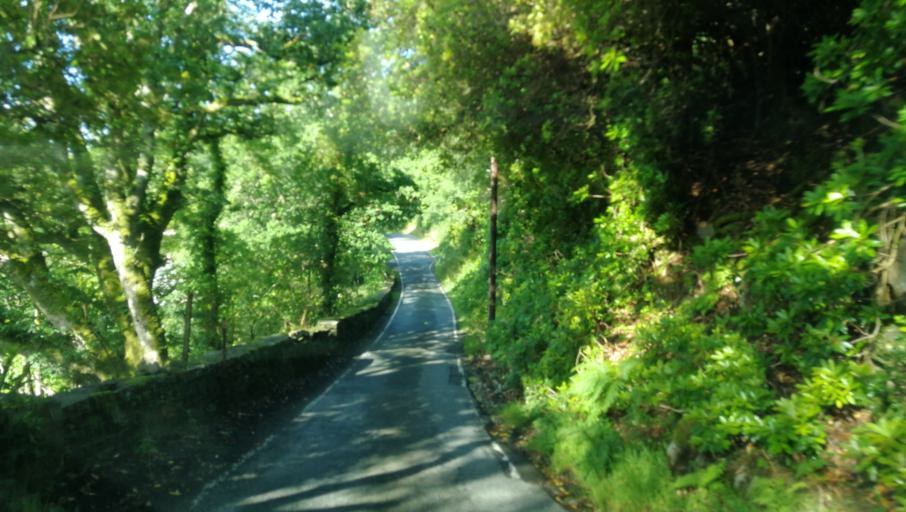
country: GB
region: Scotland
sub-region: Argyll and Bute
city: Isle Of Mull
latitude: 56.6835
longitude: -5.8250
